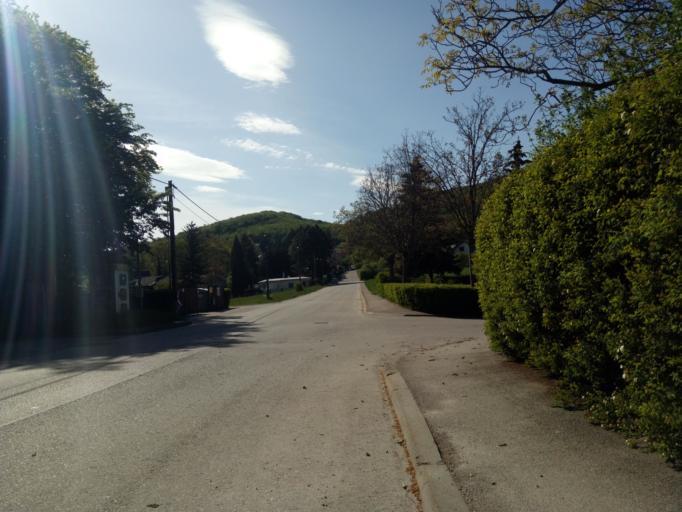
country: AT
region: Lower Austria
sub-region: Politischer Bezirk Modling
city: Kaltenleutgeben
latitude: 48.1386
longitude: 16.1918
